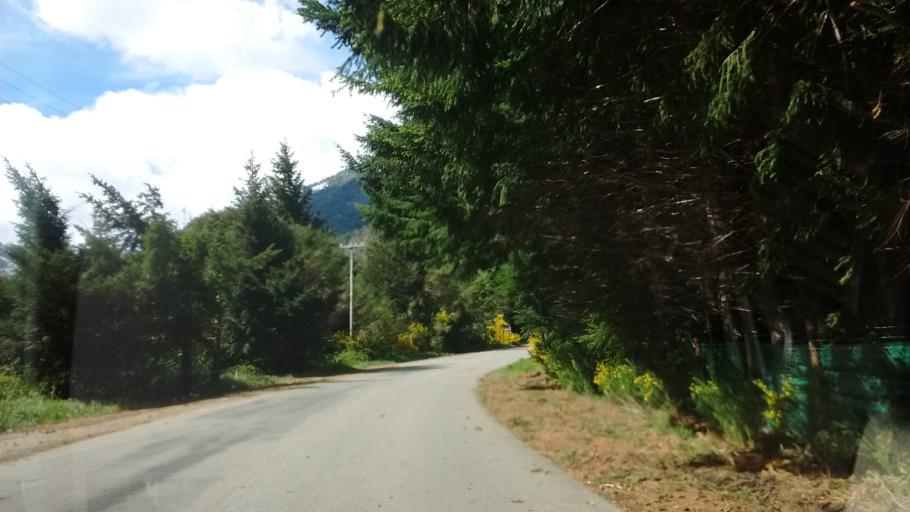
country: AR
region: Rio Negro
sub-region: Departamento de Bariloche
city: San Carlos de Bariloche
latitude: -41.0779
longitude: -71.5447
